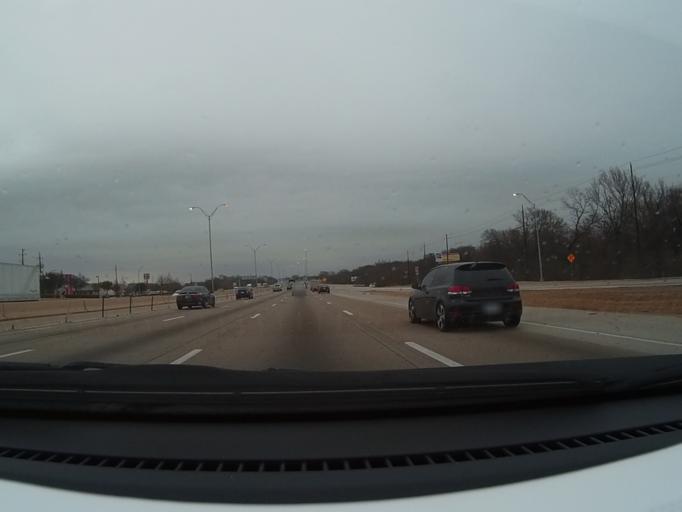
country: US
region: Texas
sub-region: Collin County
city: Allen
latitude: 33.0702
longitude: -96.6883
